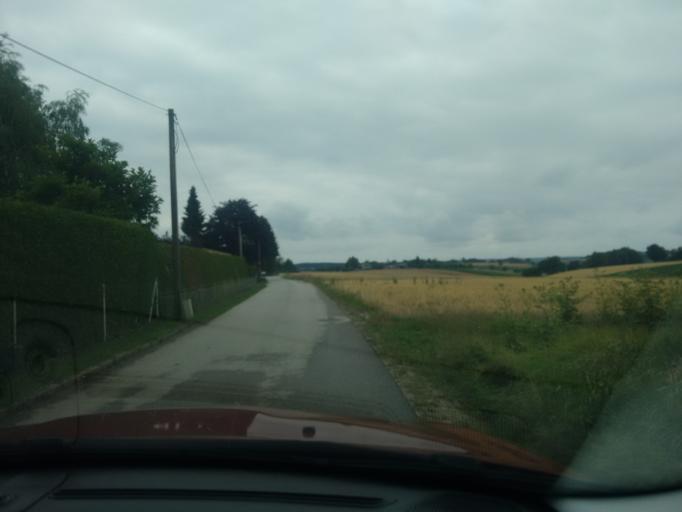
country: AT
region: Upper Austria
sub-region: Politischer Bezirk Steyr-Land
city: Bad Hall
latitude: 48.0395
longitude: 14.2303
